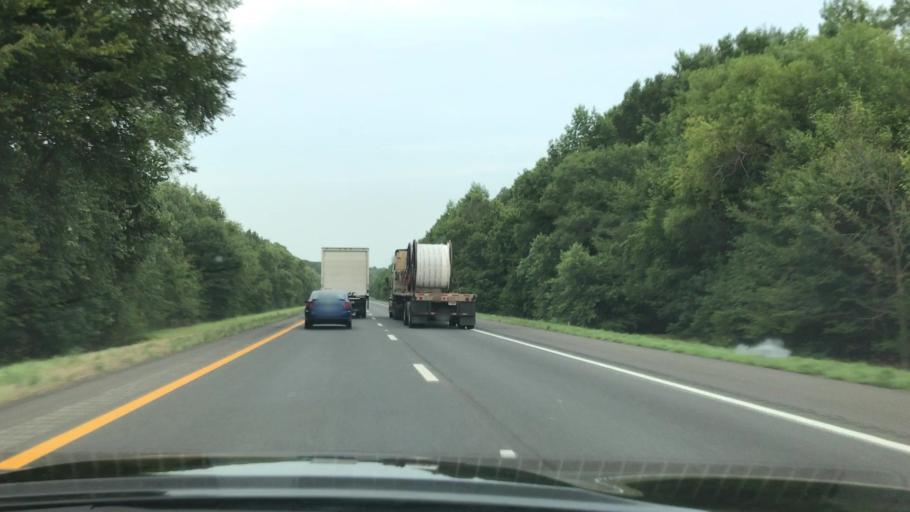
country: US
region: Texas
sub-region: Harrison County
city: Marshall
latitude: 32.4876
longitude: -94.4551
